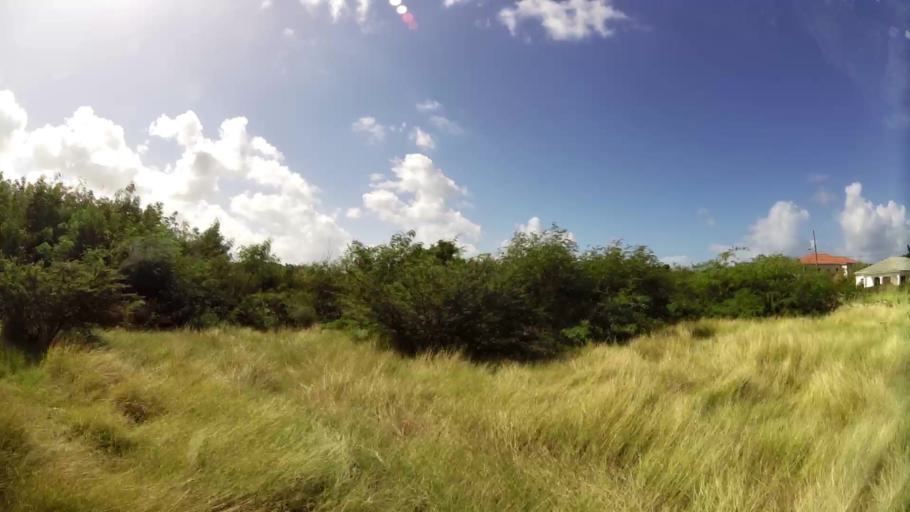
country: AG
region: Saint George
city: Piggotts
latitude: 17.1665
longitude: -61.8062
